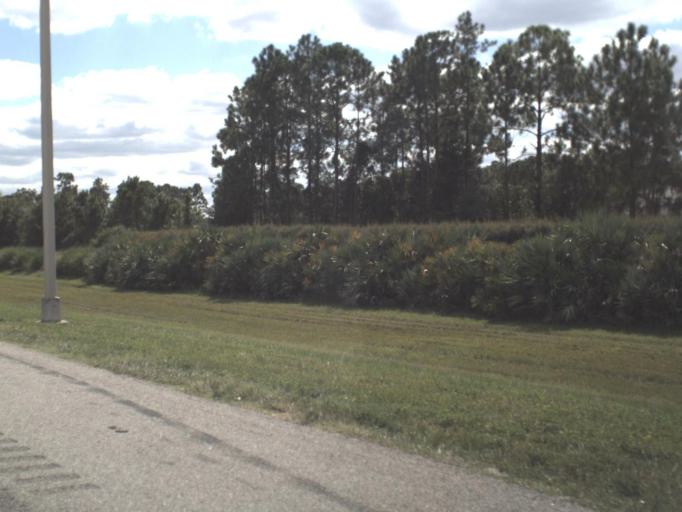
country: US
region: Florida
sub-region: Orange County
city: Tangelo Park
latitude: 28.4668
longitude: -81.4391
